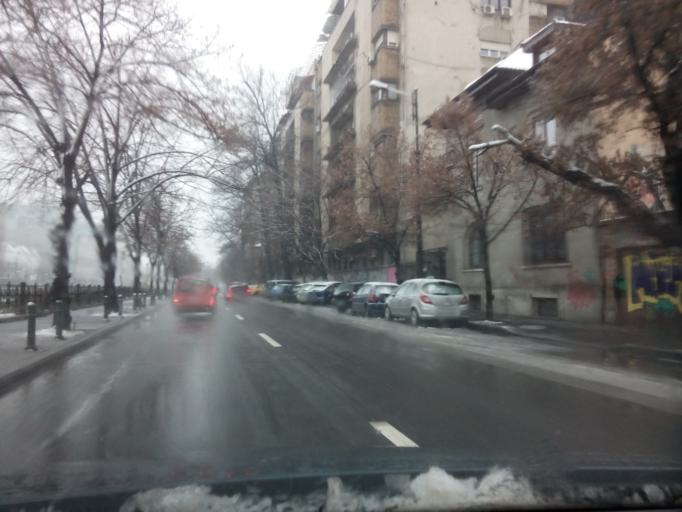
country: RO
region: Bucuresti
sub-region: Municipiul Bucuresti
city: Bucuresti
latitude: 44.4340
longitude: 26.0832
